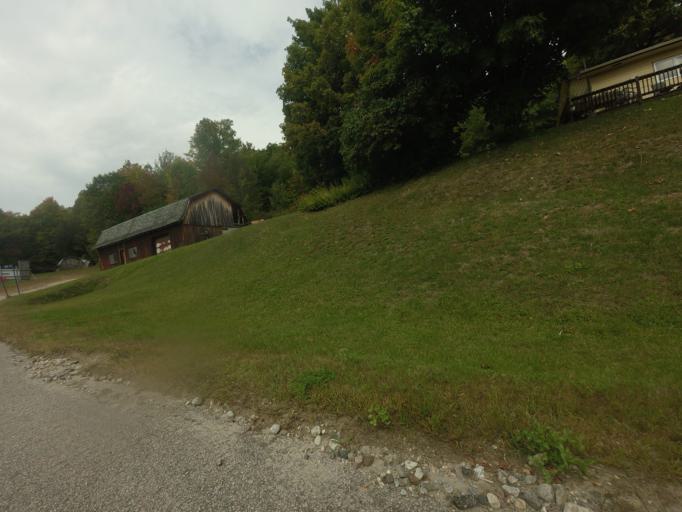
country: CA
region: Quebec
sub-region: Outaouais
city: Wakefield
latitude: 45.9477
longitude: -75.9495
